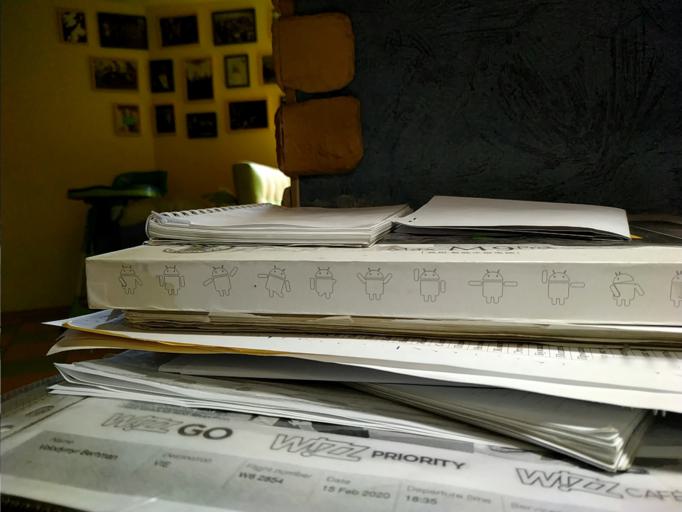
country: RU
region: Pskov
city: Plyussa
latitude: 58.5492
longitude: 29.4855
